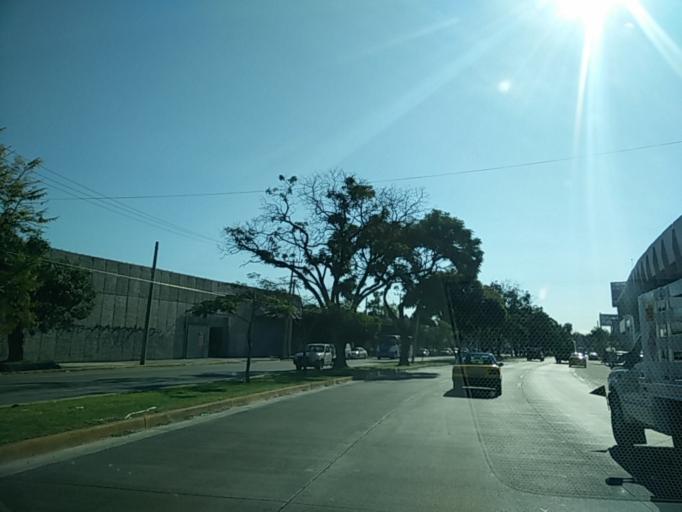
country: MX
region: Jalisco
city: Guadalajara
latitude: 20.6567
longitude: -103.3495
